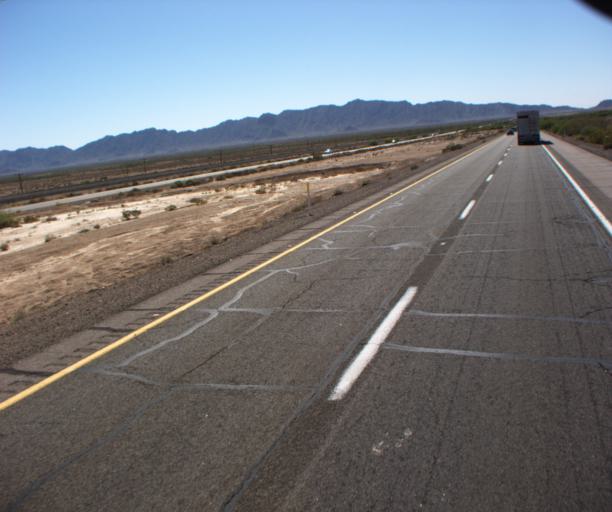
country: US
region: Arizona
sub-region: Yuma County
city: Wellton
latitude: 32.7571
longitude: -113.6456
